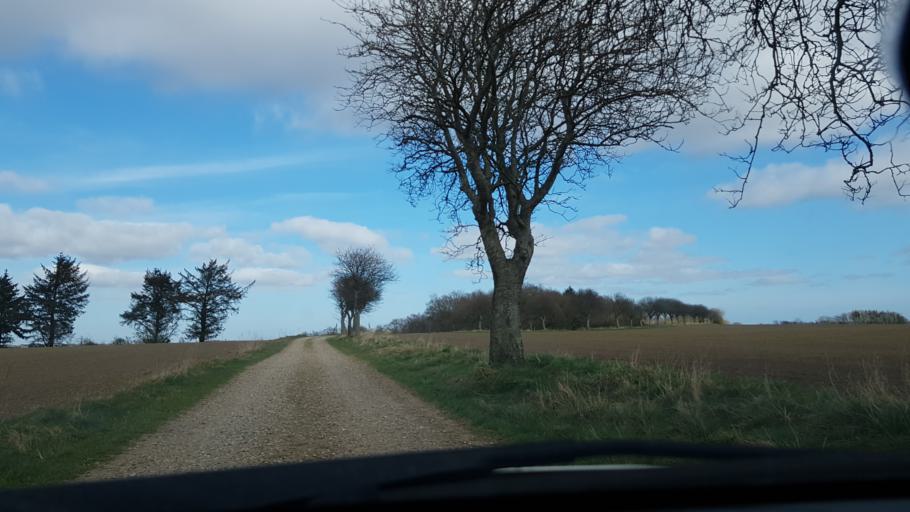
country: DK
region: South Denmark
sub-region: Vejen Kommune
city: Brorup
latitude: 55.4251
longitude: 9.0281
